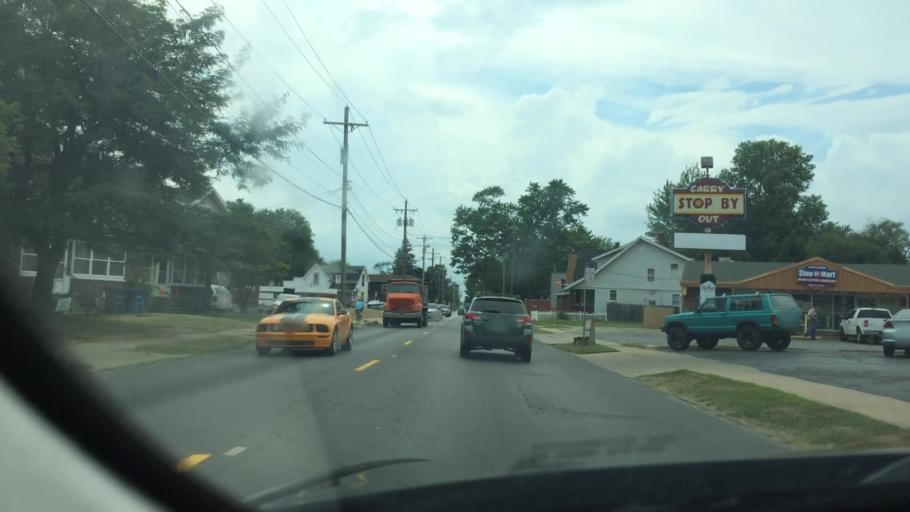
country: US
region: Ohio
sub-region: Wood County
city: Rossford
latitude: 41.6305
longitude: -83.5998
